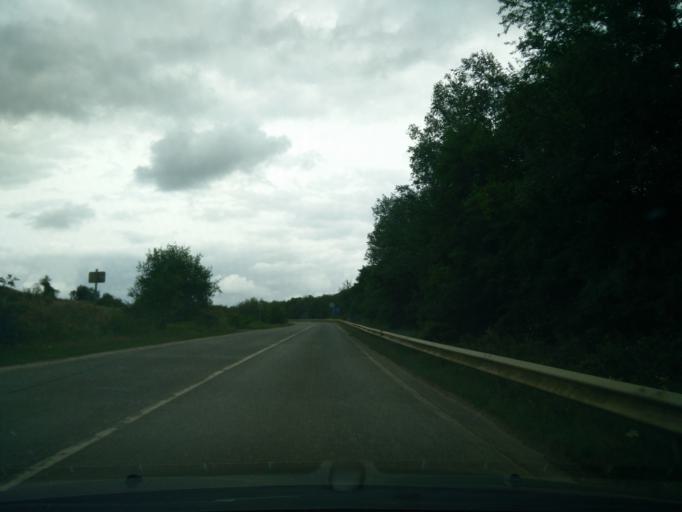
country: BE
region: Wallonia
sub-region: Province de Liege
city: Bassenge
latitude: 50.7869
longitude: 5.6389
